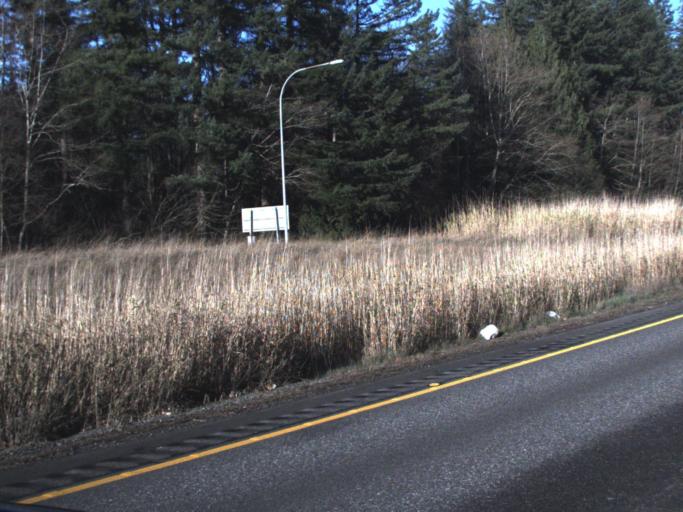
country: US
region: Washington
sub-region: Skagit County
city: Burlington
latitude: 48.5877
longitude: -122.3446
